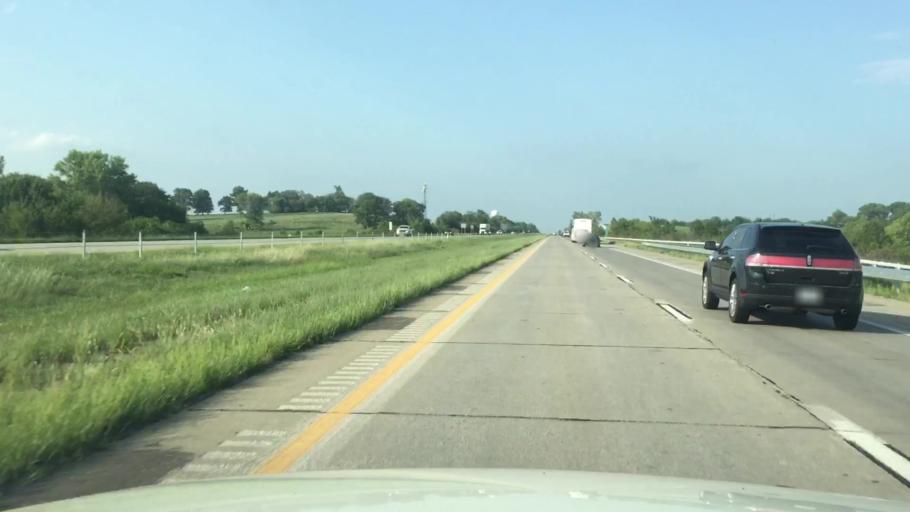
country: US
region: Missouri
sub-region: Clay County
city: Liberty
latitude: 39.2869
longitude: -94.4156
